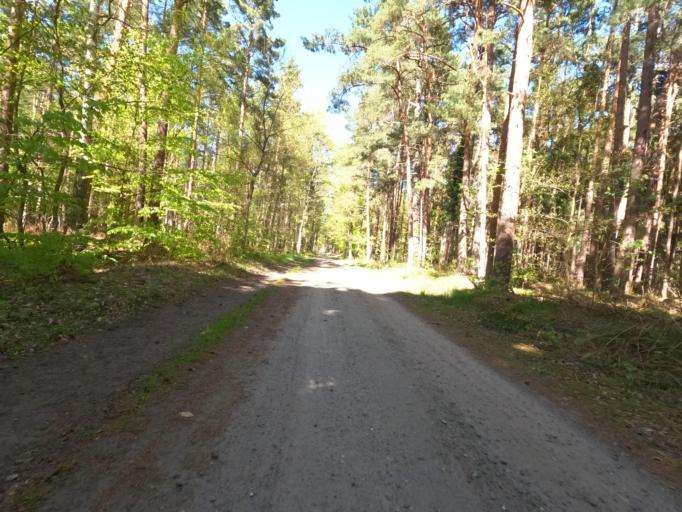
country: DE
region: Mecklenburg-Vorpommern
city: Born
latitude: 54.3934
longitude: 12.5241
